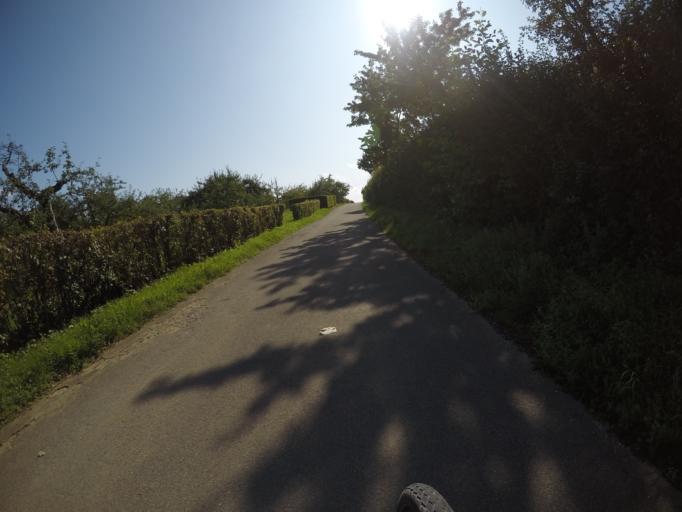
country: DE
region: Baden-Wuerttemberg
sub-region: Regierungsbezirk Stuttgart
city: Denkendorf
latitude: 48.6904
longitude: 9.3325
